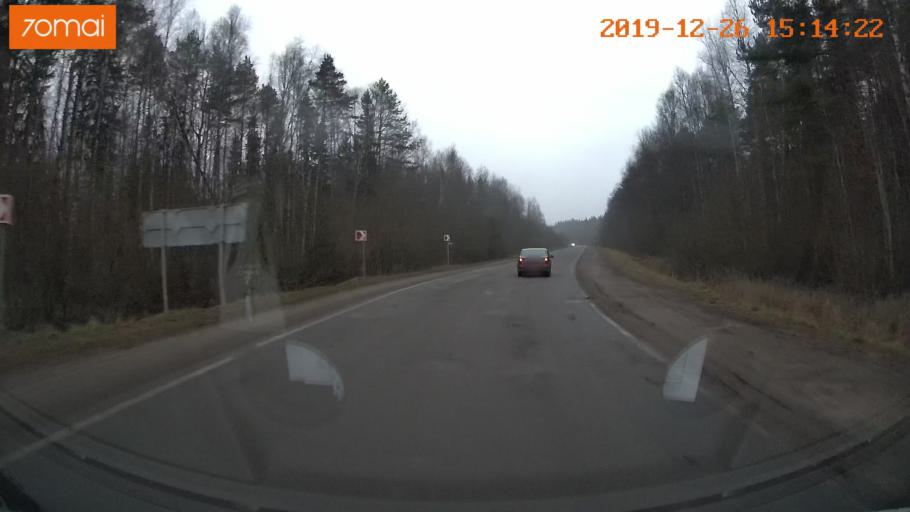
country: RU
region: Jaroslavl
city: Rybinsk
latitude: 58.1066
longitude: 38.8811
